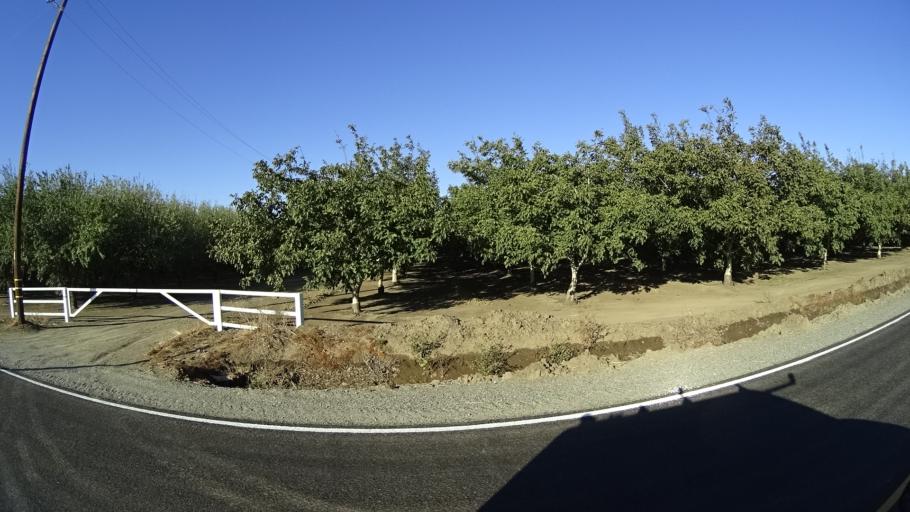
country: US
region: California
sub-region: Yolo County
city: Davis
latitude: 38.5794
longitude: -121.7859
